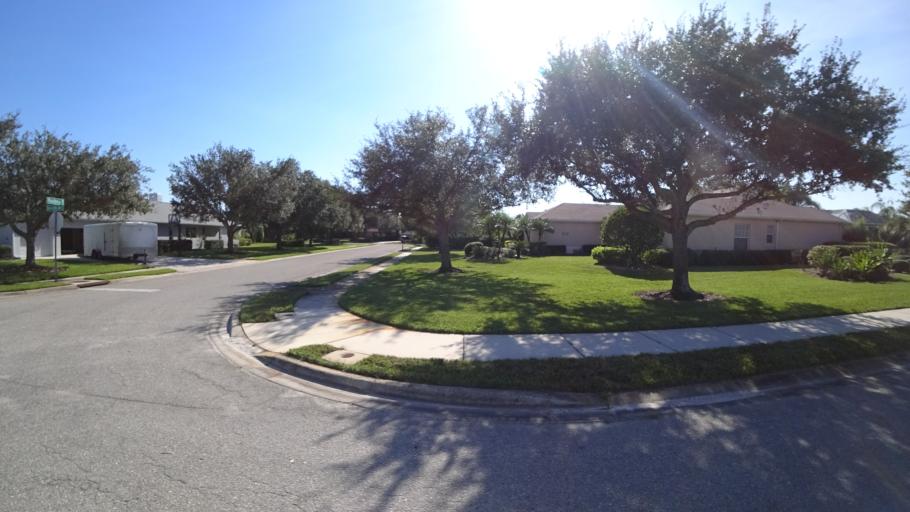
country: US
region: Florida
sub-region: Sarasota County
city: The Meadows
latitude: 27.4082
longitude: -82.4444
